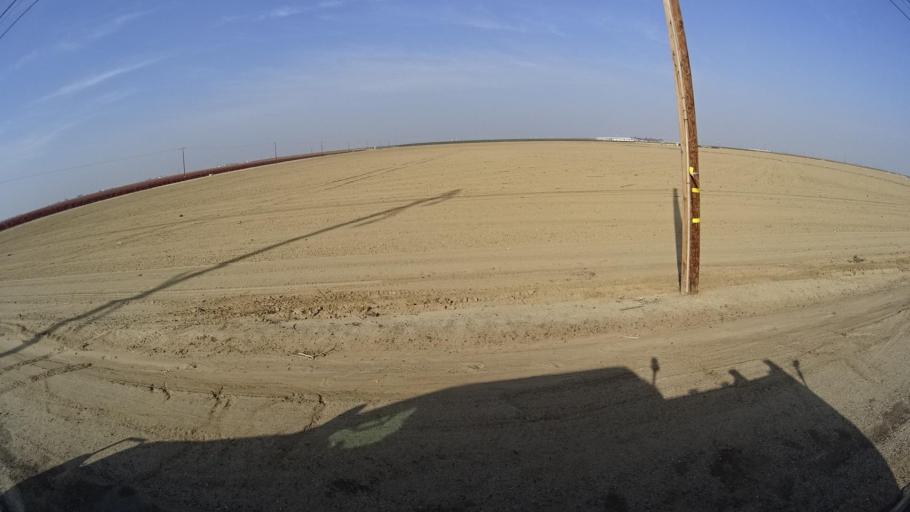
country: US
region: California
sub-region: Tulare County
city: Richgrove
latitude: 35.7760
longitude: -119.1684
